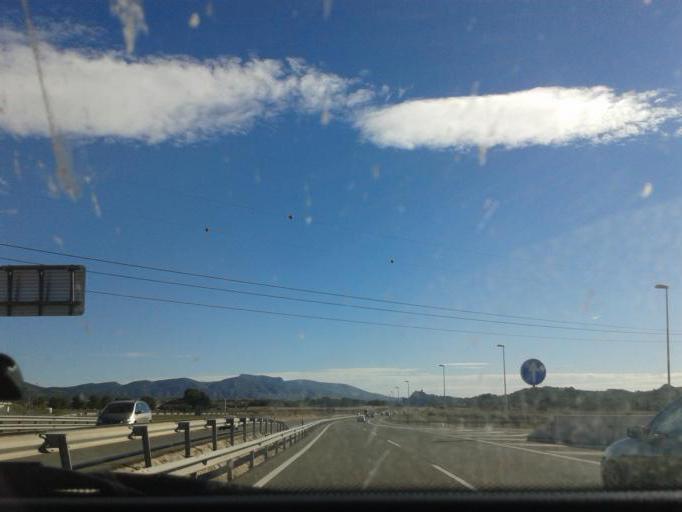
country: ES
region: Valencia
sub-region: Provincia de Alicante
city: Sax
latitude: 38.5730
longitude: -0.8396
